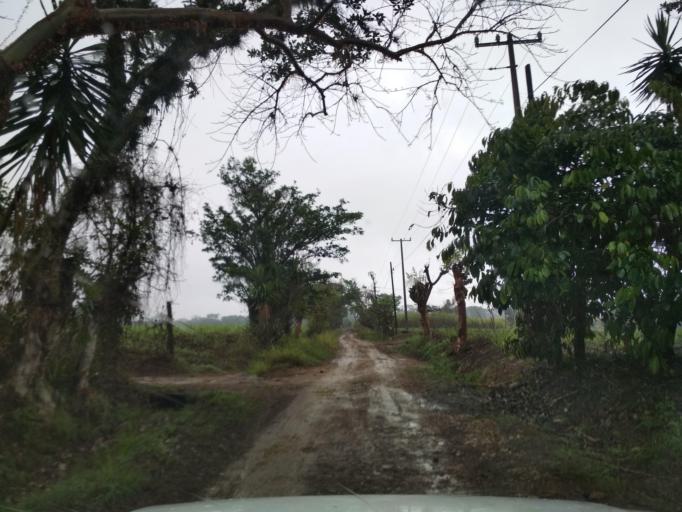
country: MX
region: Veracruz
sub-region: Amatlan de los Reyes
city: Centro de Readaptacion Social
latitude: 18.8246
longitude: -96.9382
